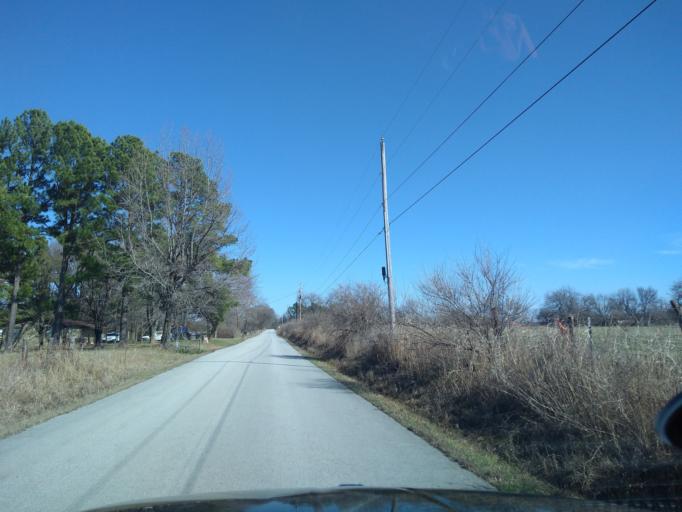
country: US
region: Arkansas
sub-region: Washington County
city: Farmington
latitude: 36.0610
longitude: -94.2472
